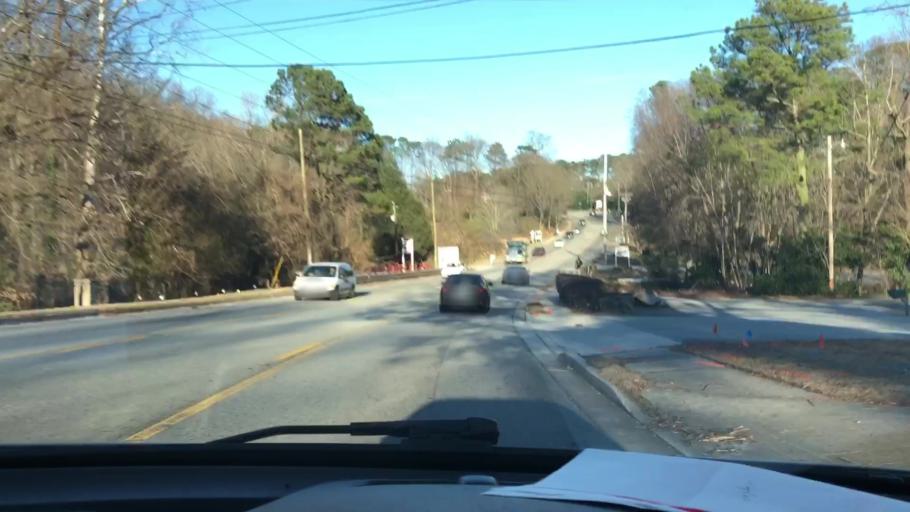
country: US
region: Georgia
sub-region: Gwinnett County
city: Snellville
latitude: 33.8956
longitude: -84.0549
